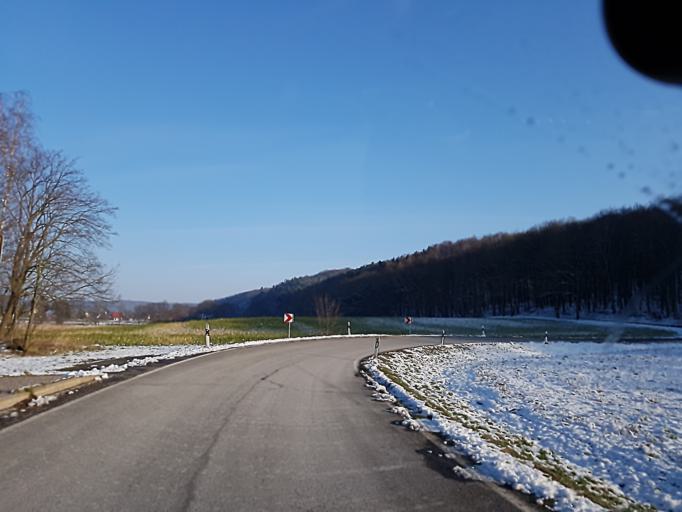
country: DE
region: Saxony
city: Leisnig
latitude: 51.1524
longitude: 12.9724
